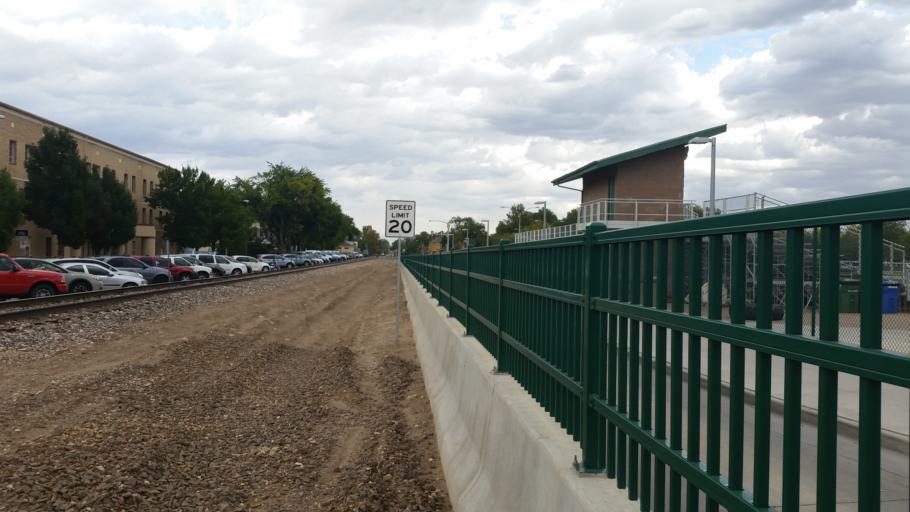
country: US
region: Colorado
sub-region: Larimer County
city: Fort Collins
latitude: 40.5712
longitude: -105.0789
